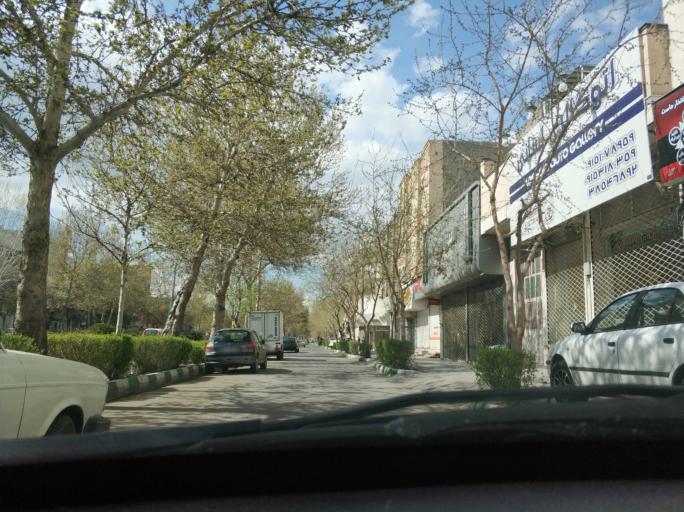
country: IR
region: Razavi Khorasan
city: Mashhad
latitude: 36.2704
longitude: 59.5965
